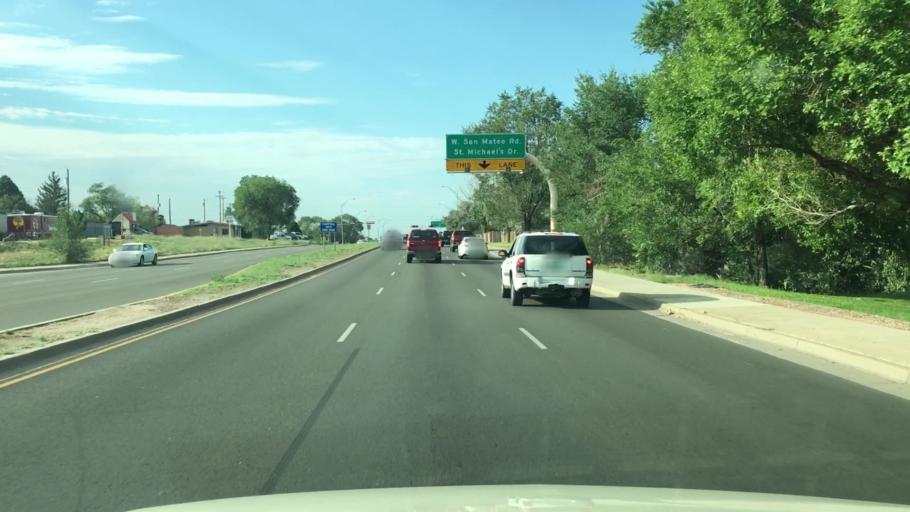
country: US
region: New Mexico
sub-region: Santa Fe County
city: Santa Fe
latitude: 35.6643
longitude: -105.9564
